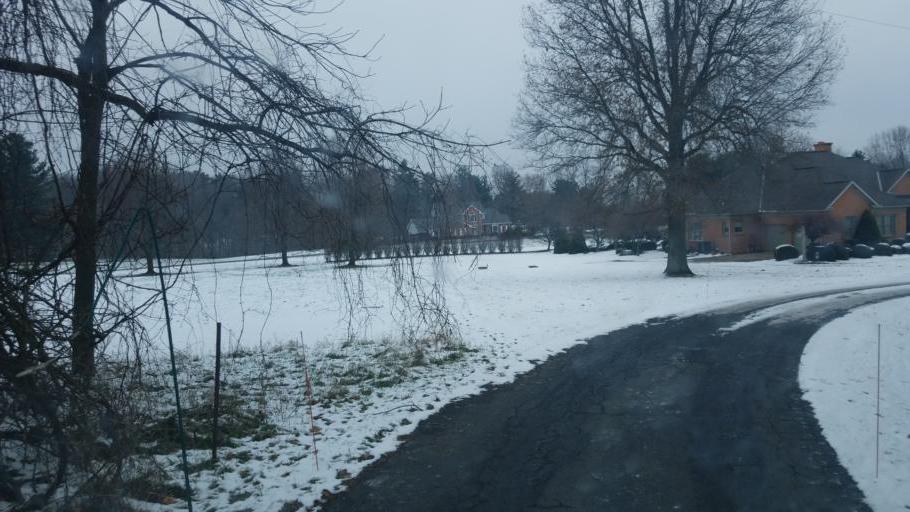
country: US
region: Ohio
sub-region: Richland County
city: Ontario
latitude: 40.7419
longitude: -82.5792
